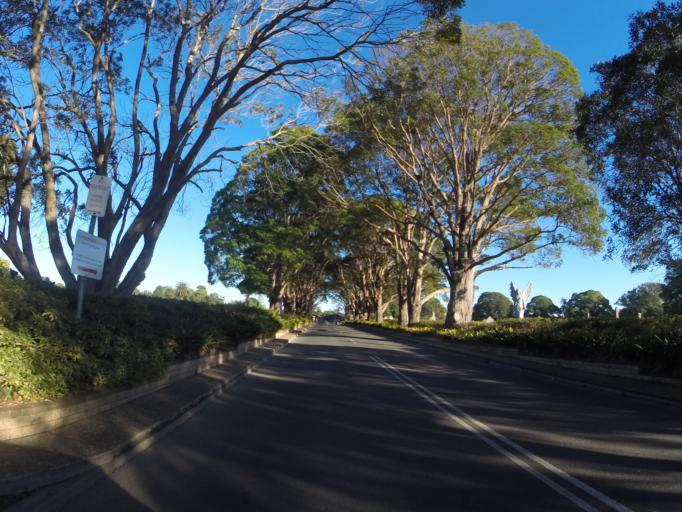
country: AU
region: New South Wales
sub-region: Sutherland Shire
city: Loftus
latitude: -34.0332
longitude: 151.0527
